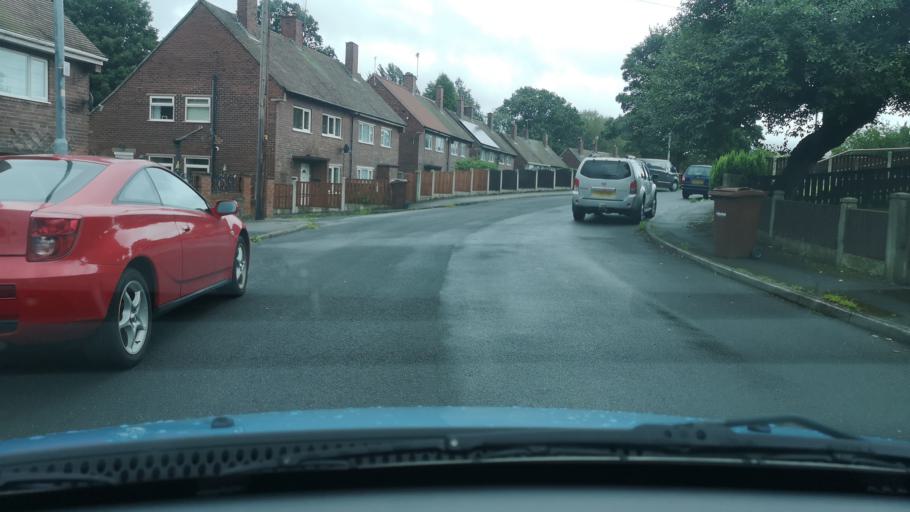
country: GB
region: England
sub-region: City and Borough of Wakefield
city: Low Ackworth
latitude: 53.6460
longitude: -1.3376
